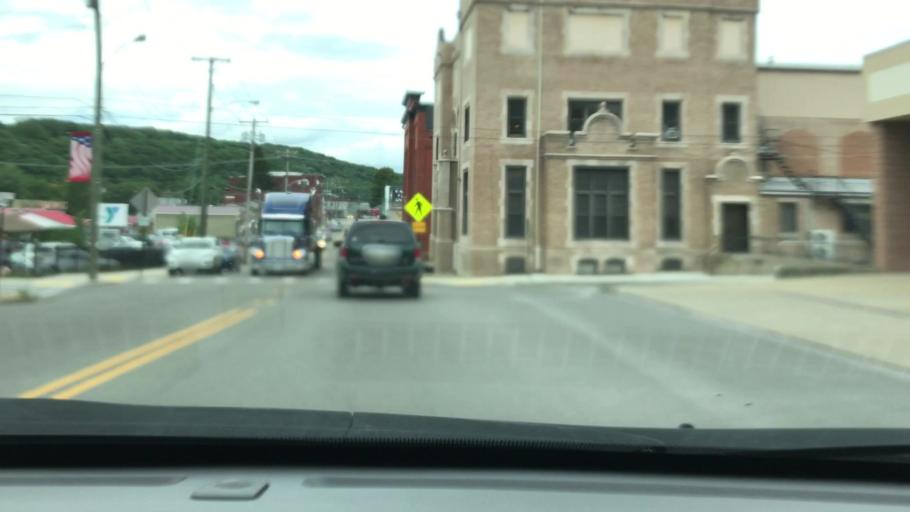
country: US
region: Pennsylvania
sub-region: Elk County
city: Ridgway
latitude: 41.4226
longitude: -78.7297
